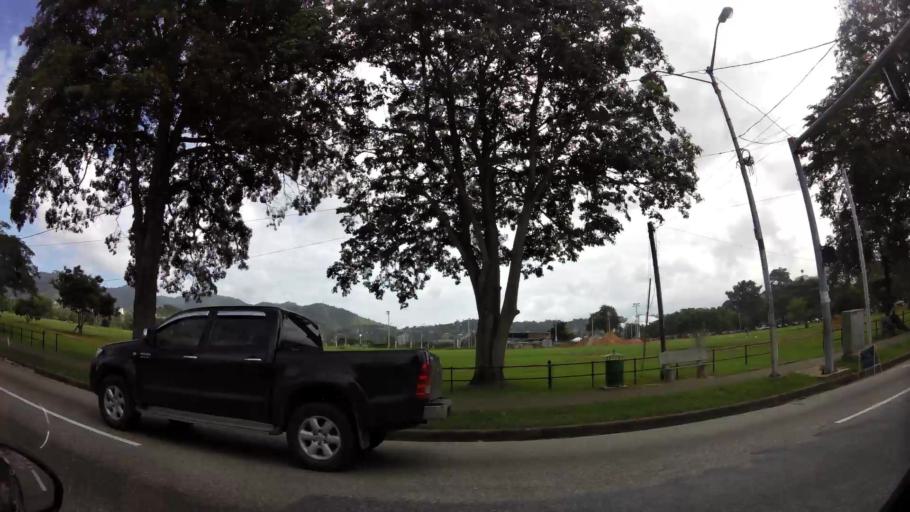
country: TT
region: City of Port of Spain
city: Port-of-Spain
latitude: 10.6659
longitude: -61.5165
